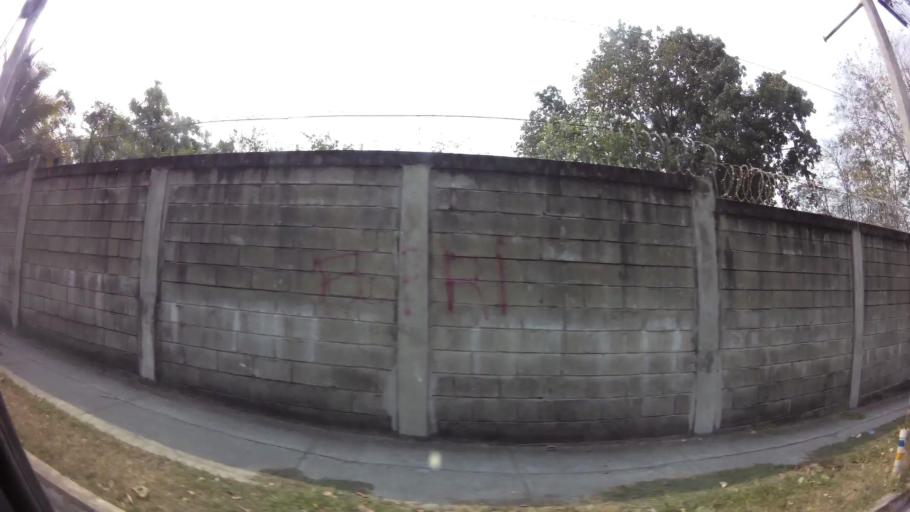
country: HN
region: Cortes
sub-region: San Pedro Sula
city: Pena Blanca
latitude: 15.5661
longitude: -88.0286
